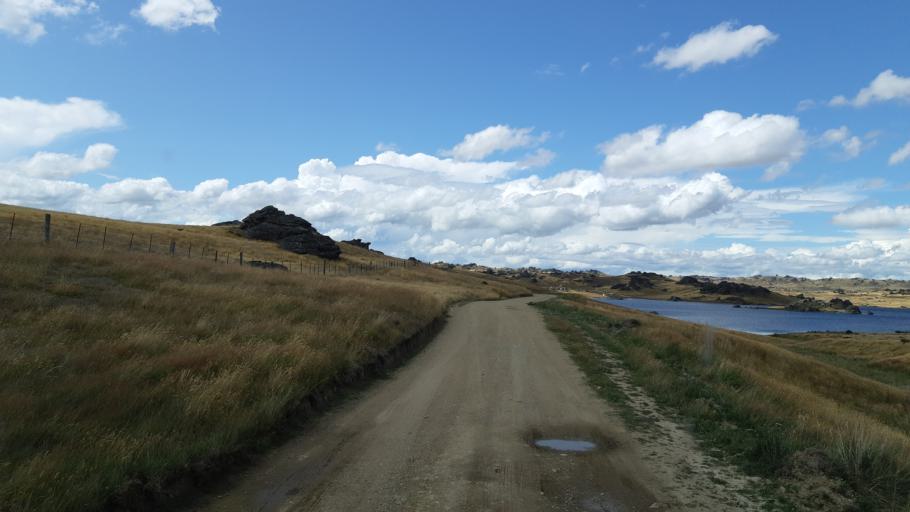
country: NZ
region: Otago
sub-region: Queenstown-Lakes District
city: Wanaka
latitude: -45.2958
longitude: 169.7330
